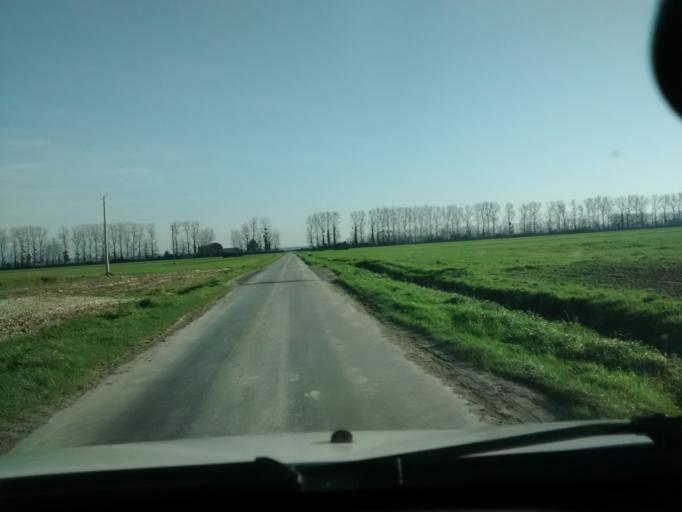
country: FR
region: Brittany
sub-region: Departement d'Ille-et-Vilaine
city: Roz-sur-Couesnon
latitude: 48.5940
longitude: -1.5540
